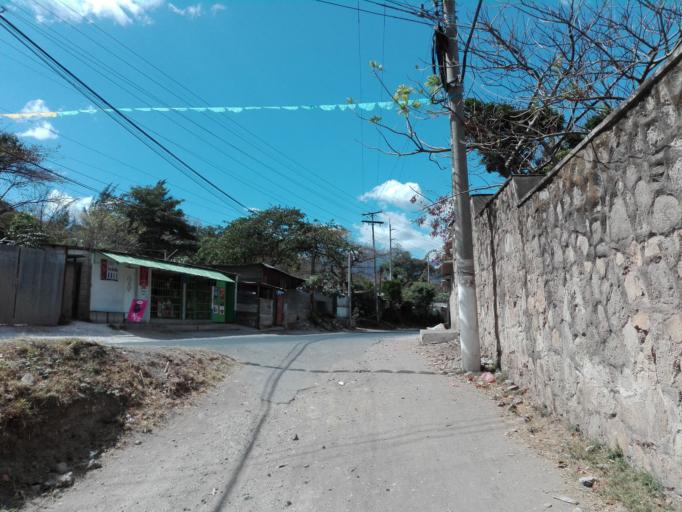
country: GT
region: Guatemala
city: Amatitlan
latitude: 14.4720
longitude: -90.6060
